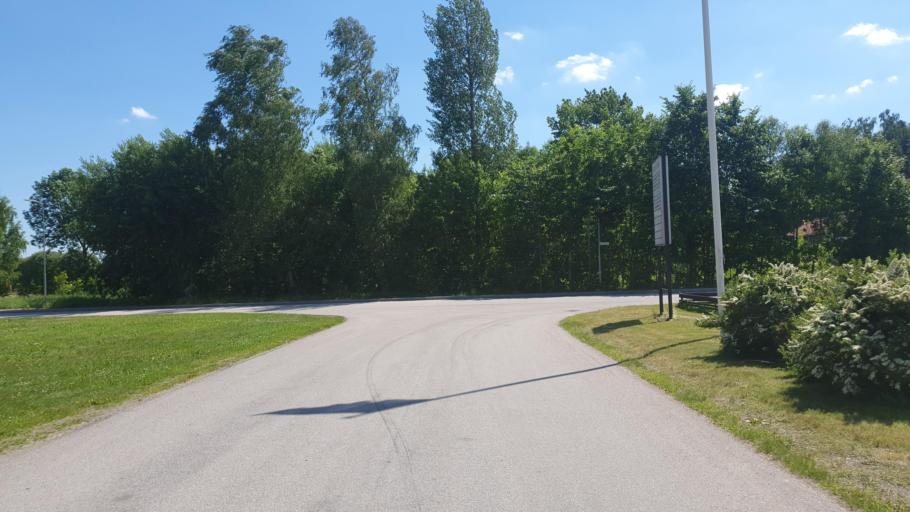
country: SE
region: Uppsala
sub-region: Osthammars Kommun
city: Gimo
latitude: 60.1756
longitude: 18.1777
